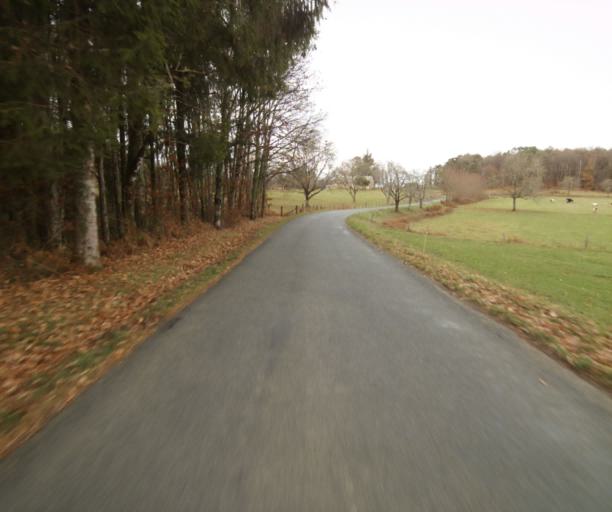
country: FR
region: Limousin
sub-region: Departement de la Correze
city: Chameyrat
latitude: 45.2532
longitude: 1.6810
